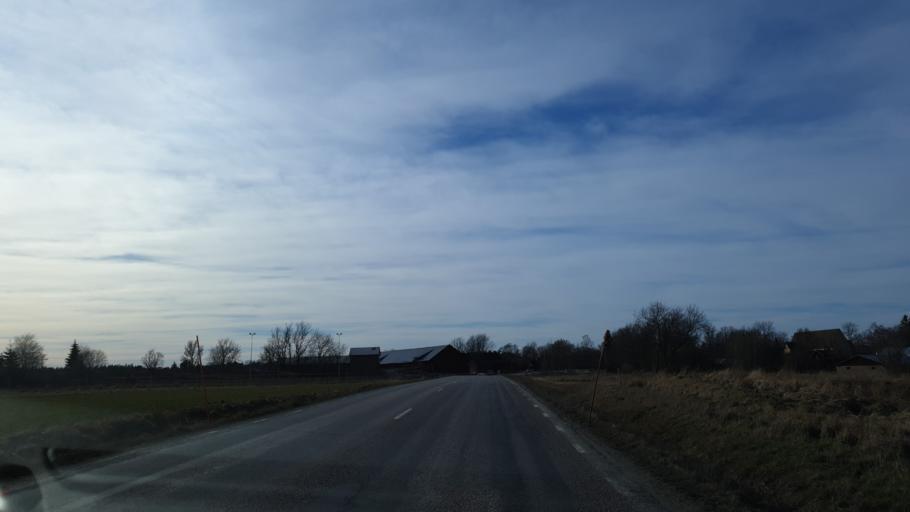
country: SE
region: Uppsala
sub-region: Enkopings Kommun
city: Grillby
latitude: 59.5939
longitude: 17.1840
